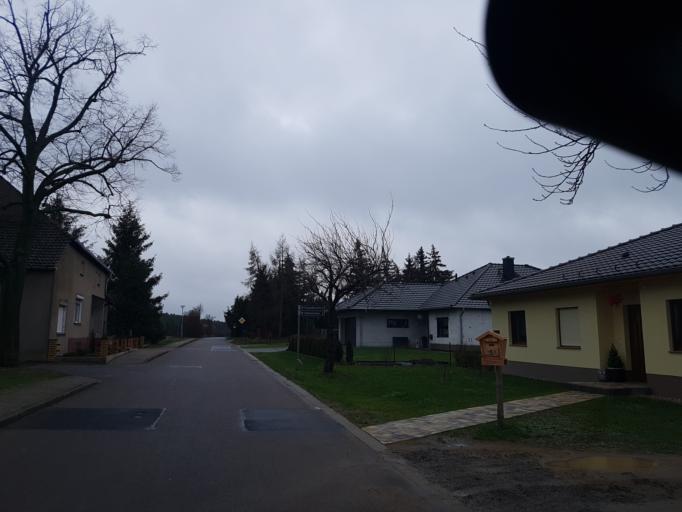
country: DE
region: Brandenburg
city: Muhlberg
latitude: 51.4655
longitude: 13.2986
